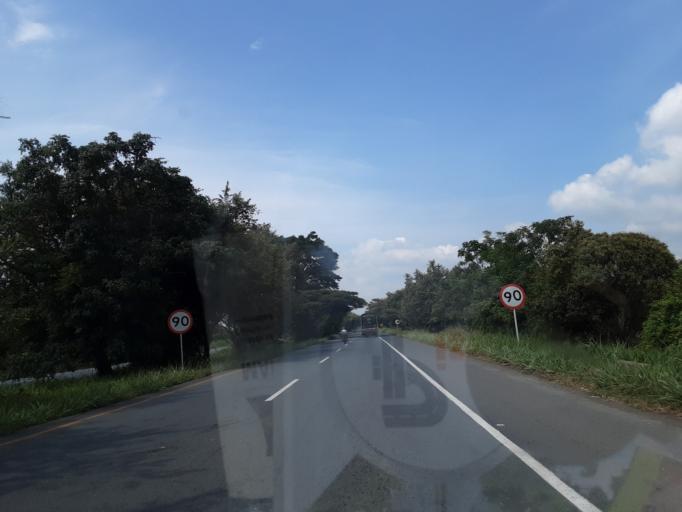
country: CO
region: Valle del Cauca
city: El Cerrito
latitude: 3.6618
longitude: -76.2927
